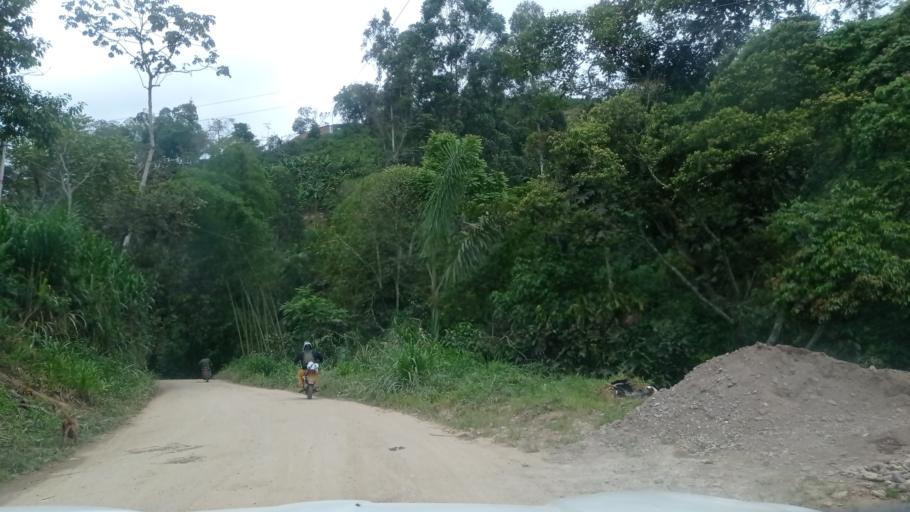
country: CO
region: Huila
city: Garzon
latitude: 2.1047
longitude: -75.6289
